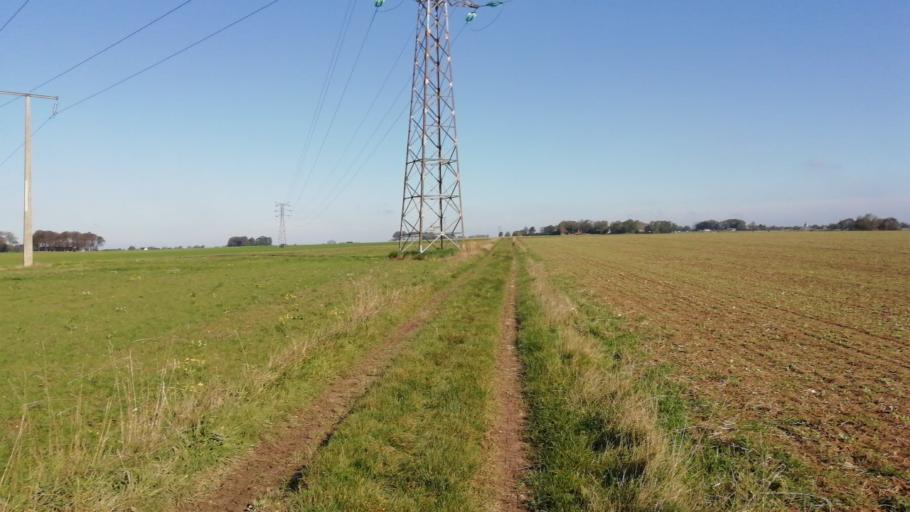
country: FR
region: Haute-Normandie
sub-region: Departement de la Seine-Maritime
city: Maneglise
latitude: 49.5771
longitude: 0.2601
